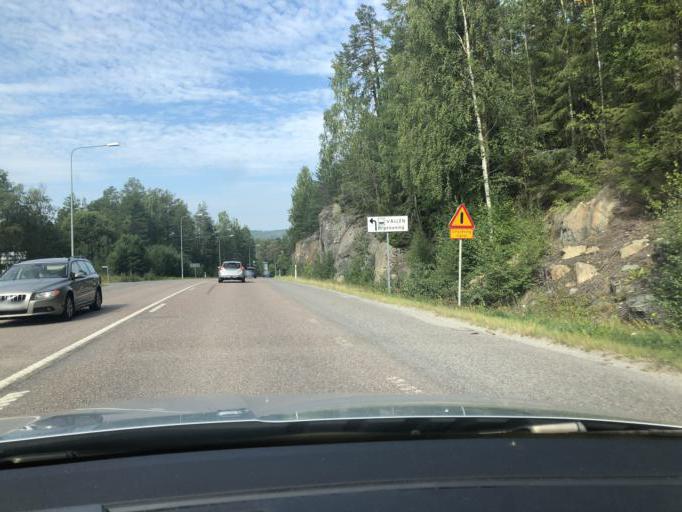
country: SE
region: Vaesternorrland
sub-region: Kramfors Kommun
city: Kramfors
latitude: 62.9126
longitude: 17.7916
